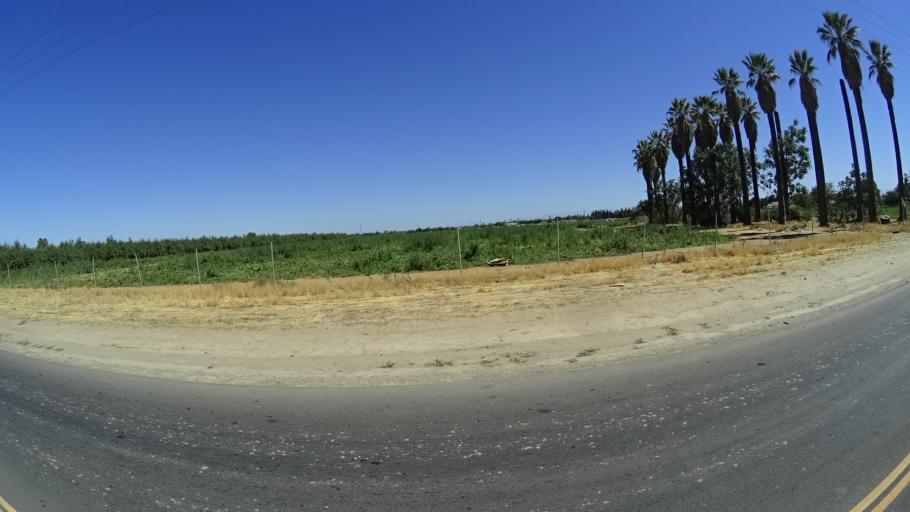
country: US
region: California
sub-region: Fresno County
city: Easton
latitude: 36.6922
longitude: -119.8034
